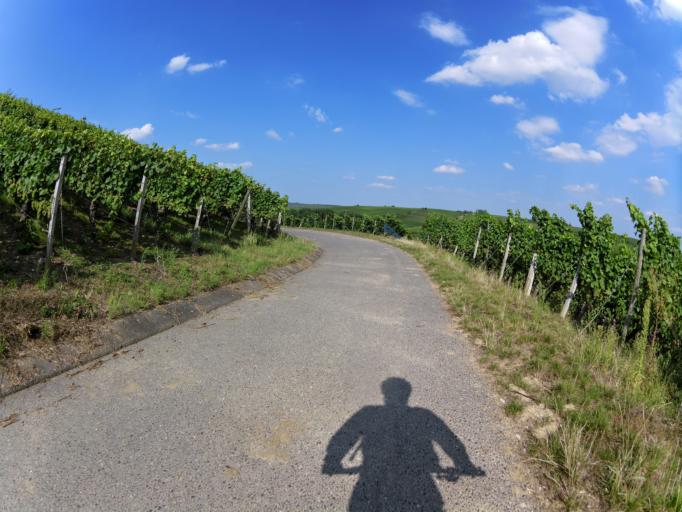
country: DE
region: Bavaria
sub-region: Regierungsbezirk Unterfranken
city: Sommerach
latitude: 49.8355
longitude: 10.1755
